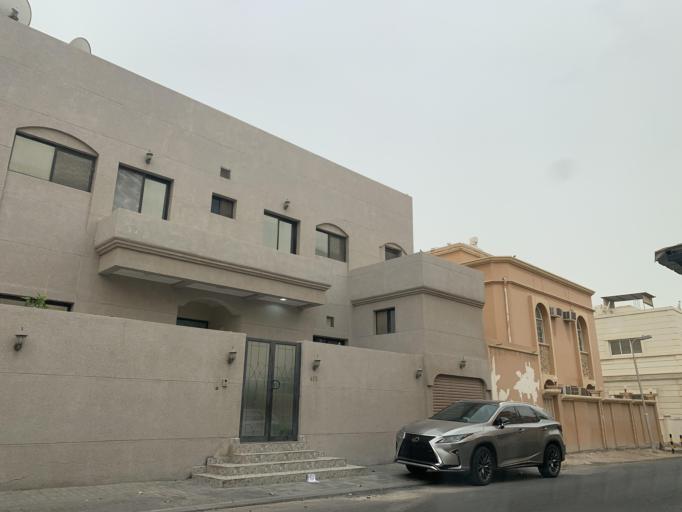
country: BH
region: Northern
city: Ar Rifa'
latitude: 26.1466
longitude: 50.5238
